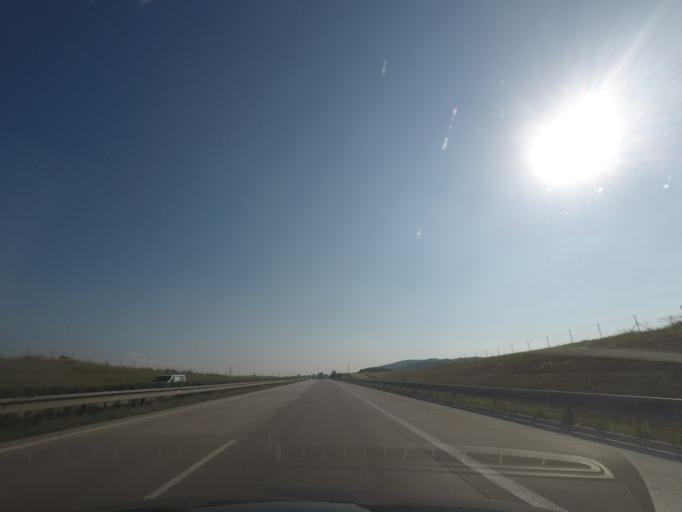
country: CZ
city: Fulnek
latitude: 49.6811
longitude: 17.9374
